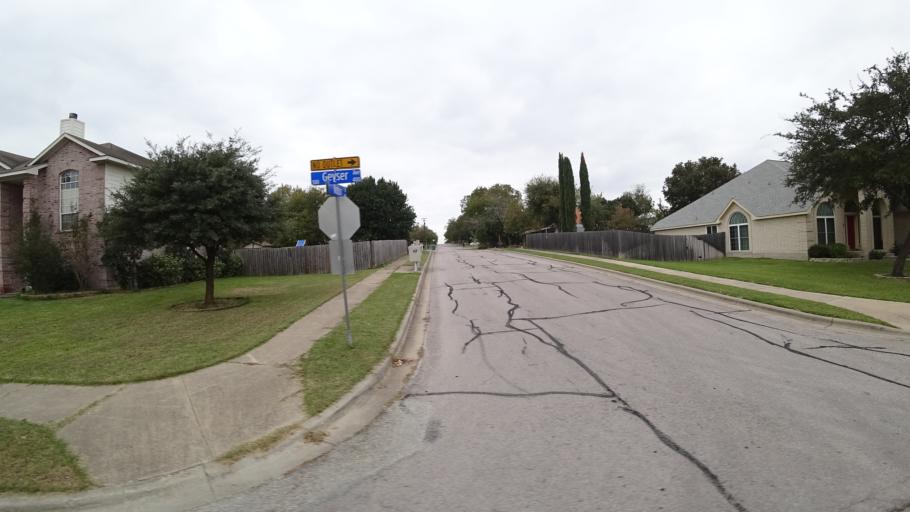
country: US
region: Texas
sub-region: Travis County
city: Pflugerville
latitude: 30.4357
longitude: -97.6205
